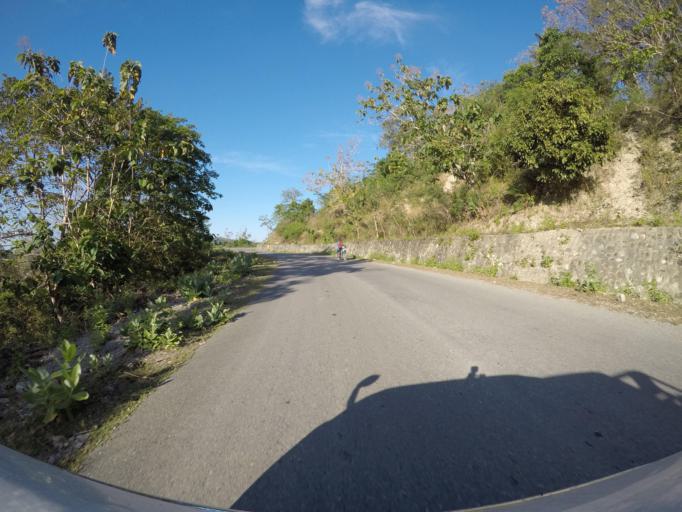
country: TL
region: Viqueque
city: Viqueque
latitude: -8.8738
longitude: 126.3583
